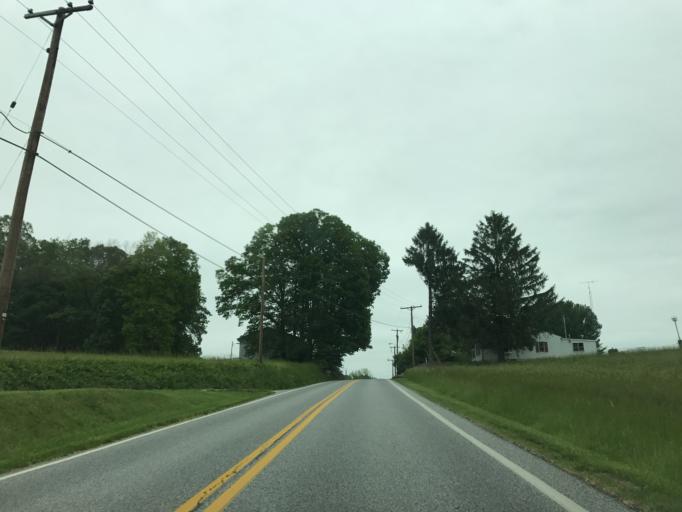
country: US
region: Pennsylvania
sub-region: York County
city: New Freedom
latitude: 39.7109
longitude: -76.6718
